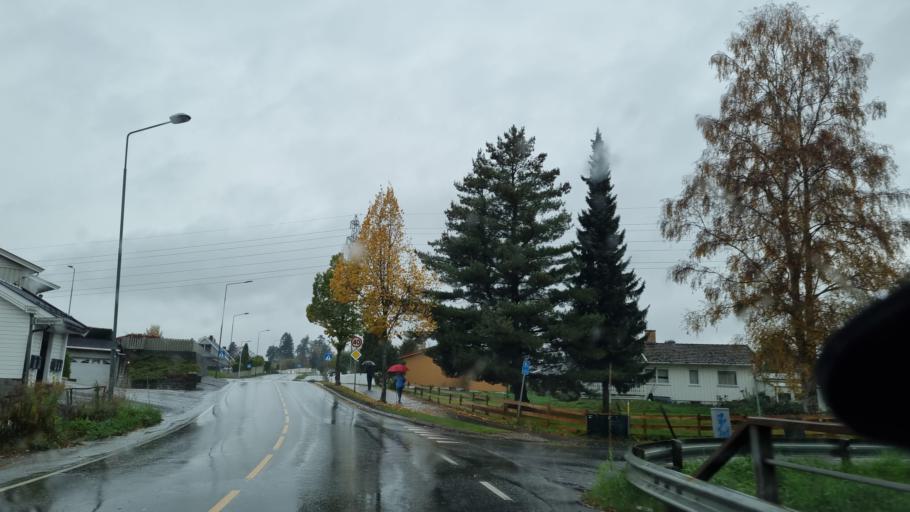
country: NO
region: Hedmark
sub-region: Hamar
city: Hamar
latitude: 60.8026
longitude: 11.1305
